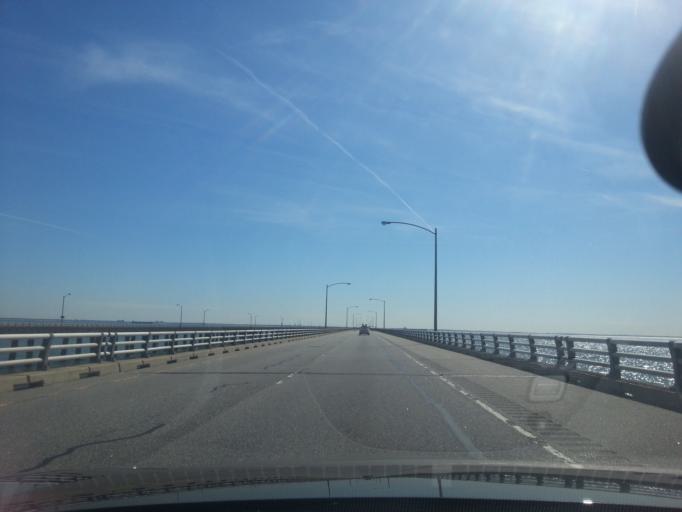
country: US
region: Virginia
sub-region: City of Virginia Beach
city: Virginia Beach
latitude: 37.0186
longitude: -76.0919
